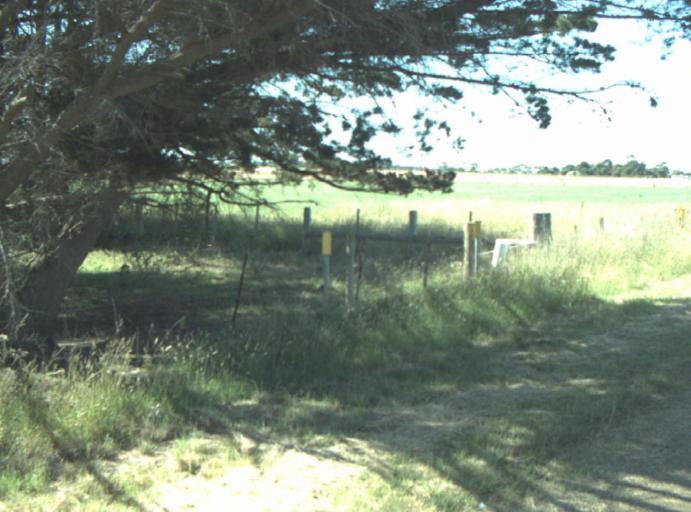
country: AU
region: Victoria
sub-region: Greater Geelong
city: Bell Post Hill
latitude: -38.0908
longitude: 144.3062
